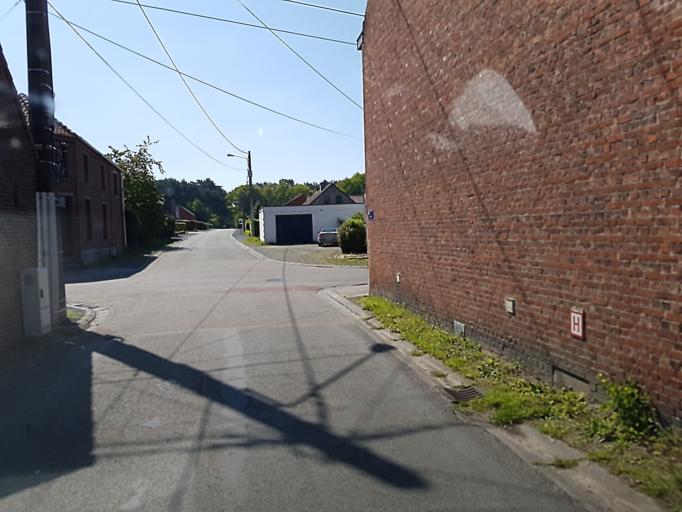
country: BE
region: Wallonia
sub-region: Province du Hainaut
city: Jurbise
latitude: 50.5080
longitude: 3.9054
